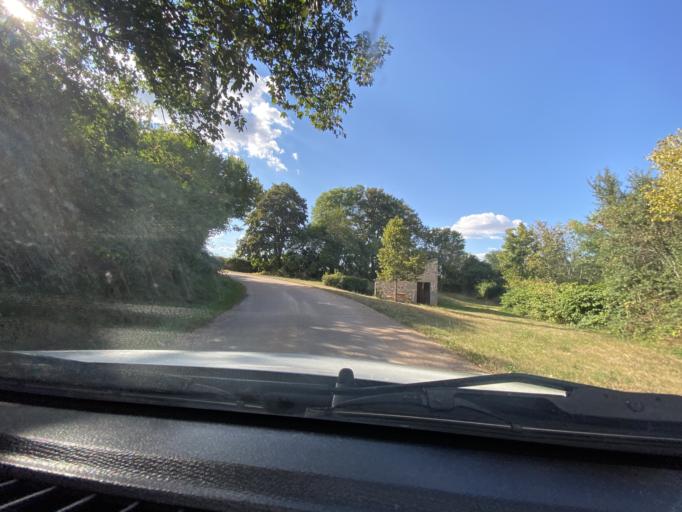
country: FR
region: Bourgogne
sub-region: Departement de la Cote-d'Or
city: Saulieu
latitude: 47.3185
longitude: 4.2020
